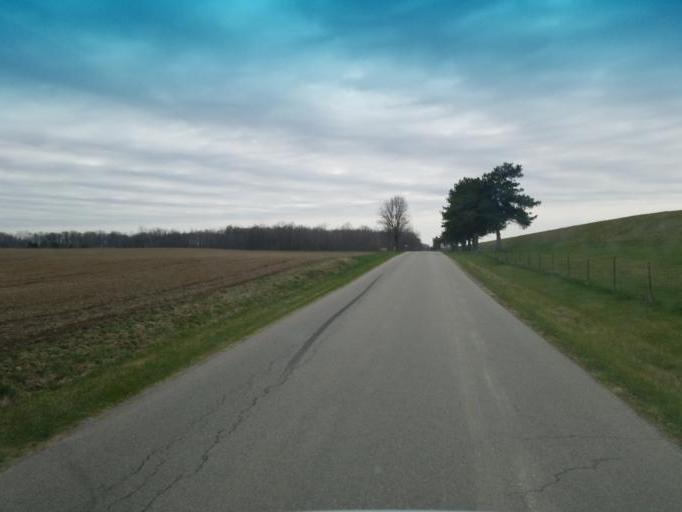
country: US
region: Ohio
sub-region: Crawford County
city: Bucyrus
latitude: 40.8322
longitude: -82.9306
